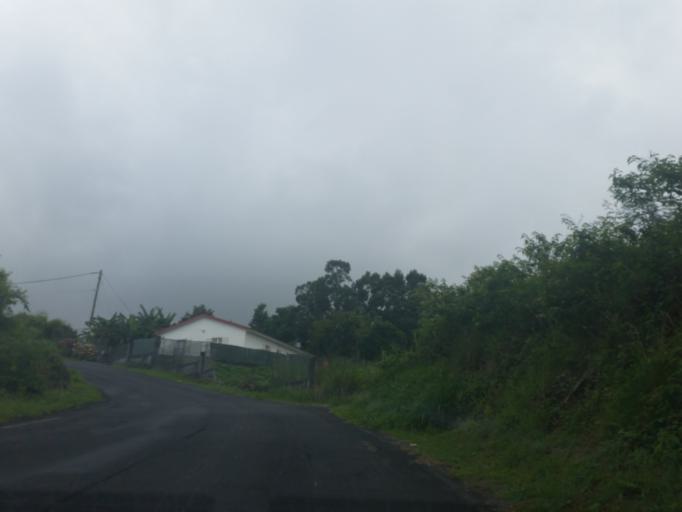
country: RE
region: Reunion
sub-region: Reunion
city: Le Tampon
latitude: -21.2406
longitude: 55.5167
